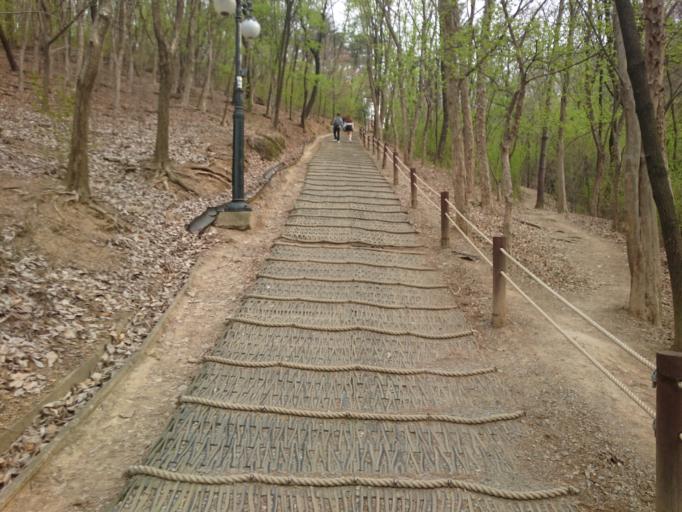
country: KR
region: Daegu
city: Daegu
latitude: 35.8494
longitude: 128.5594
